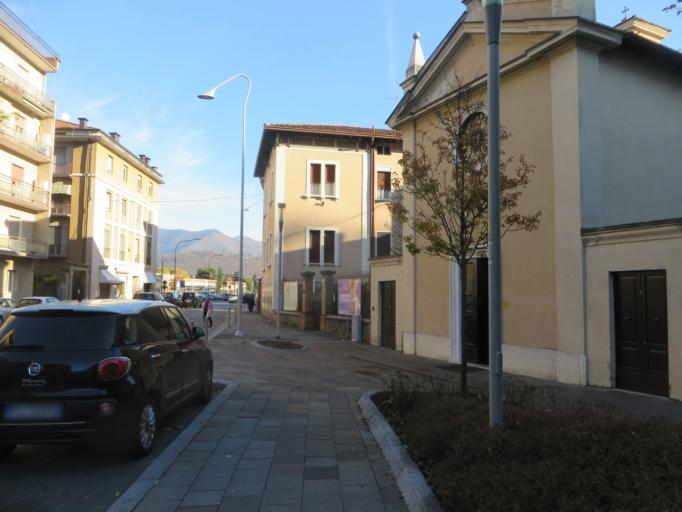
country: IT
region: Lombardy
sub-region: Provincia di Brescia
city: Brescia
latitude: 45.5538
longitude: 10.2316
